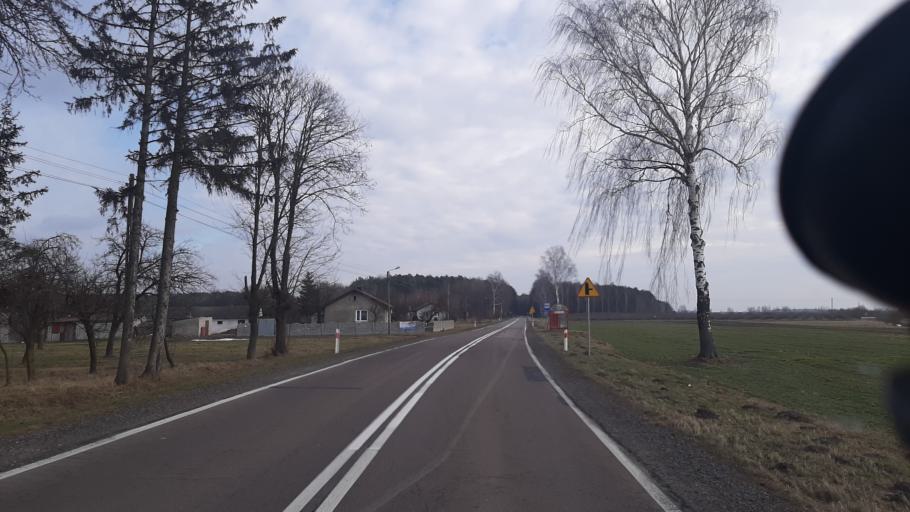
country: PL
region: Lublin Voivodeship
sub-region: Powiat lubartowski
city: Ostrow Lubelski
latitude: 51.4918
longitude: 22.7872
